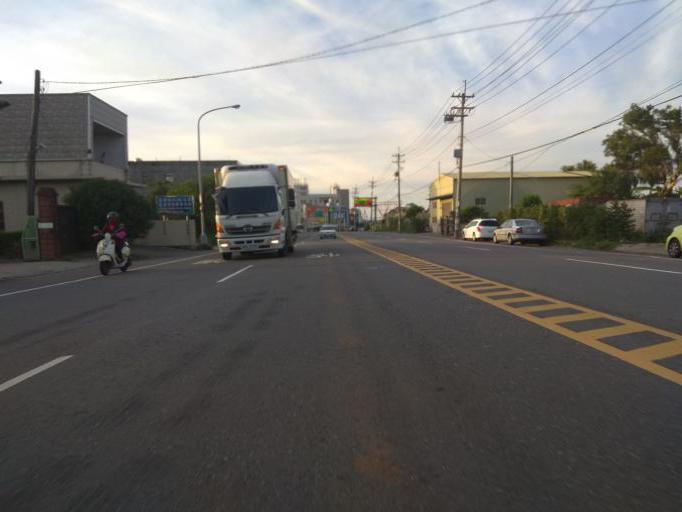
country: TW
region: Taiwan
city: Taoyuan City
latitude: 24.9817
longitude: 121.1913
